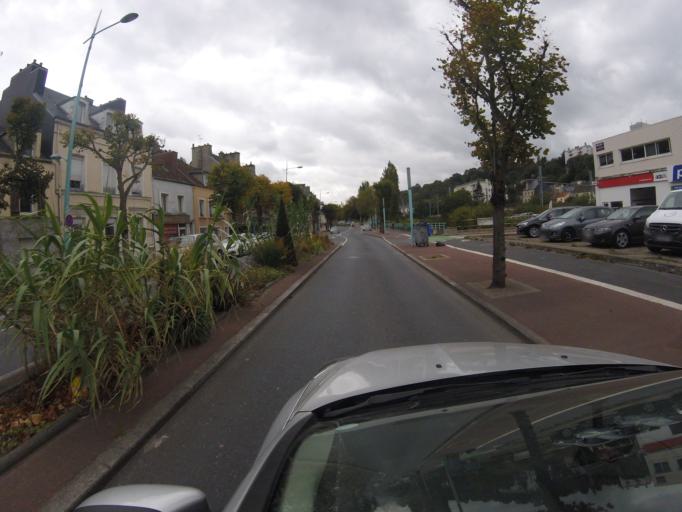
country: FR
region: Lower Normandy
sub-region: Departement de la Manche
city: Cherbourg-Octeville
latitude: 49.6294
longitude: -1.6181
